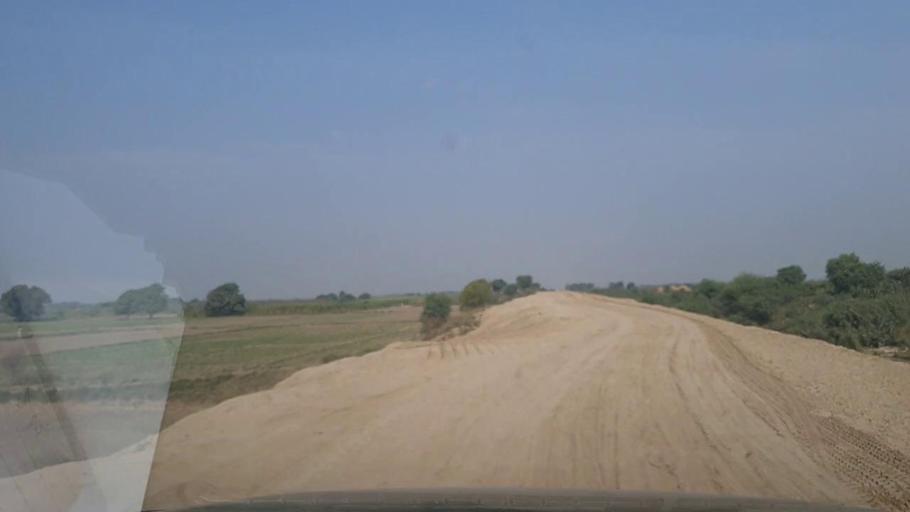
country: PK
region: Sindh
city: Bulri
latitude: 24.9900
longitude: 68.2928
